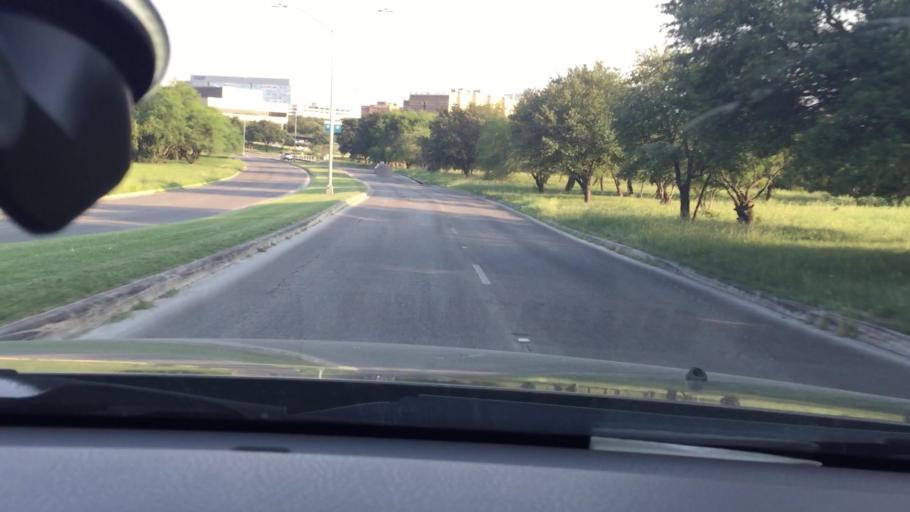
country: US
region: Texas
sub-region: Bexar County
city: Leon Valley
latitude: 29.5175
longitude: -98.5861
